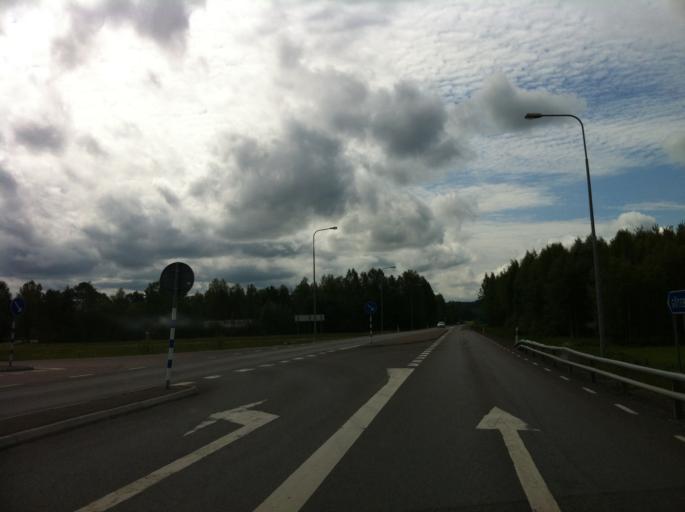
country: SE
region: Vaermland
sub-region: Sunne Kommun
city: Sunne
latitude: 59.7353
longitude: 13.1319
